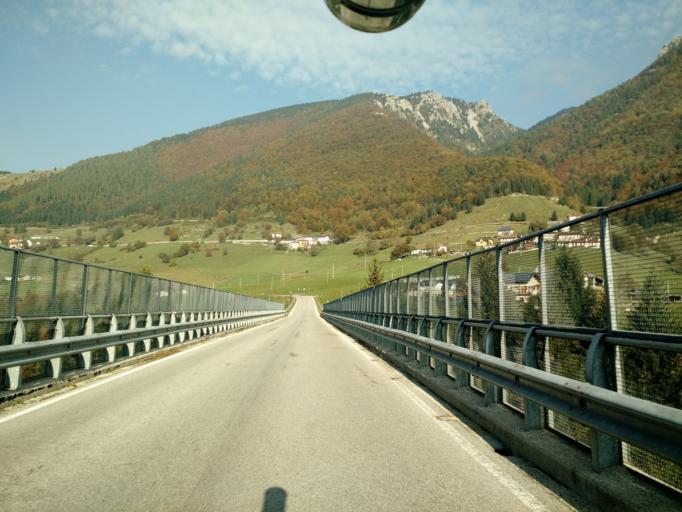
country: IT
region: Veneto
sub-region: Provincia di Vicenza
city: Foza
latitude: 45.8888
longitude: 11.6047
